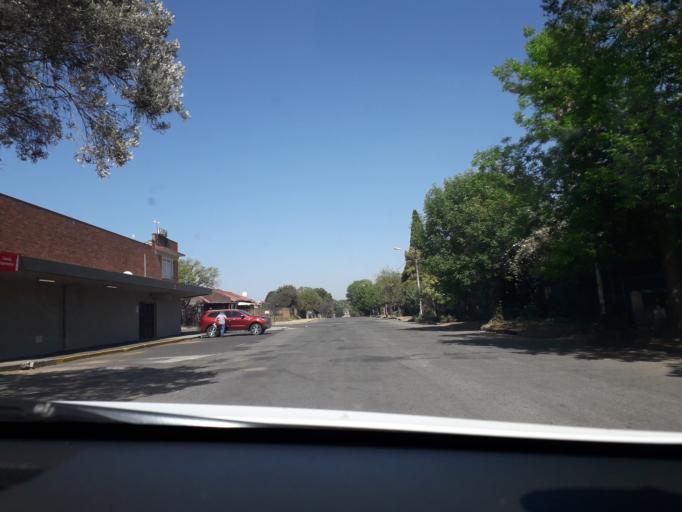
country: ZA
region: Gauteng
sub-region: City of Johannesburg Metropolitan Municipality
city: Modderfontein
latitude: -26.0916
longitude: 28.2250
